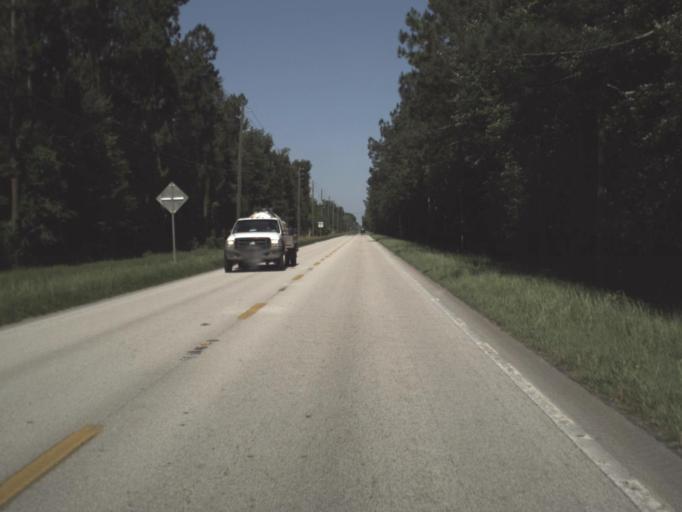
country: US
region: Florida
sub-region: Duval County
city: Baldwin
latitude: 30.3047
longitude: -81.9380
